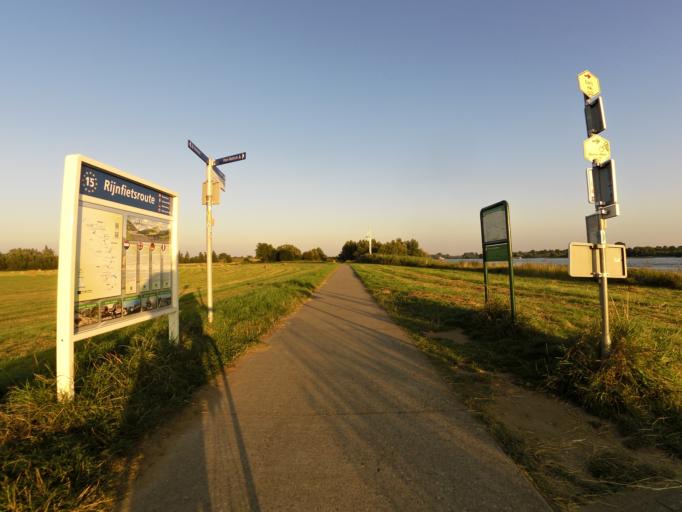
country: NL
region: Gelderland
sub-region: Gemeente Zevenaar
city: Zevenaar
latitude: 51.8687
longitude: 6.0629
